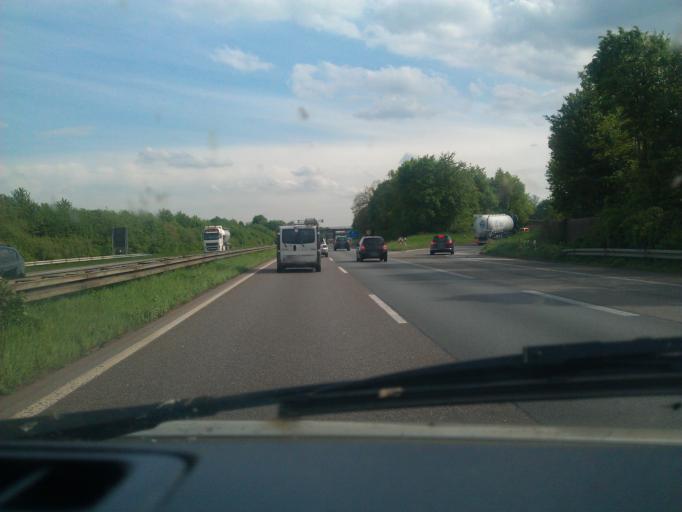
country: DE
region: North Rhine-Westphalia
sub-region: Regierungsbezirk Dusseldorf
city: Moers
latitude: 51.4726
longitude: 6.5873
